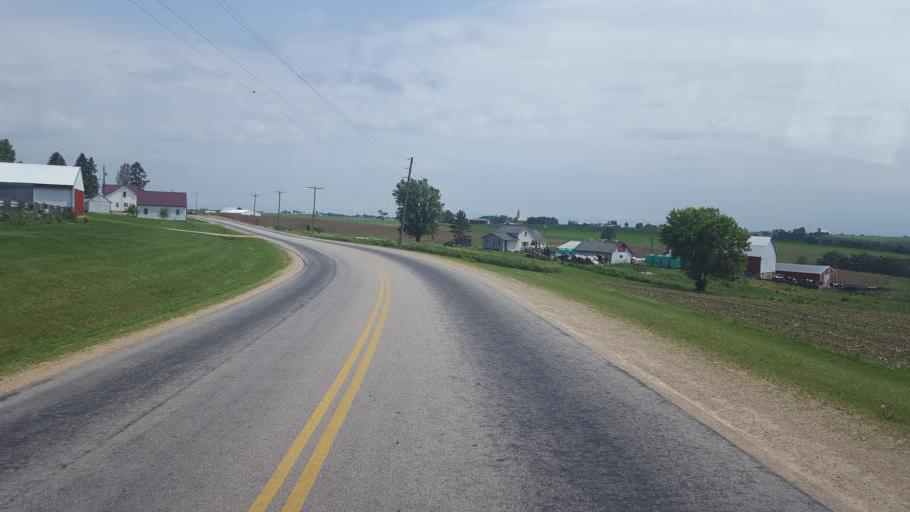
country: US
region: Wisconsin
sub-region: Monroe County
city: Cashton
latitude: 43.7881
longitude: -90.7027
